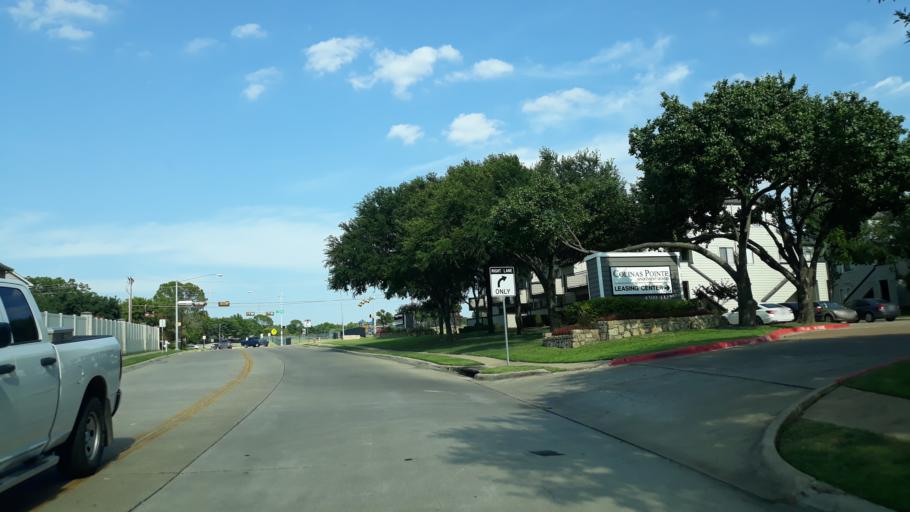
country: US
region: Texas
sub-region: Dallas County
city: Irving
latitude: 32.8408
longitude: -97.0107
